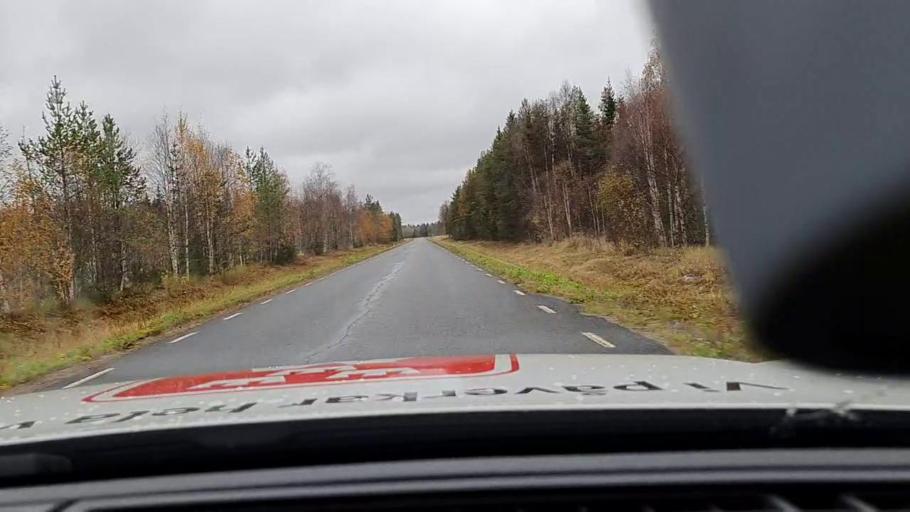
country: SE
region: Norrbotten
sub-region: Haparanda Kommun
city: Haparanda
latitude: 65.9284
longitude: 23.8180
